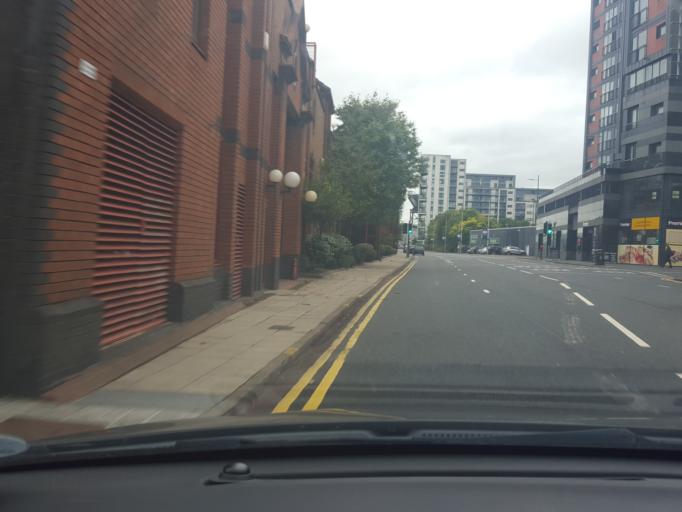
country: GB
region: Scotland
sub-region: Glasgow City
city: Glasgow
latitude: 55.8568
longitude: -4.2739
